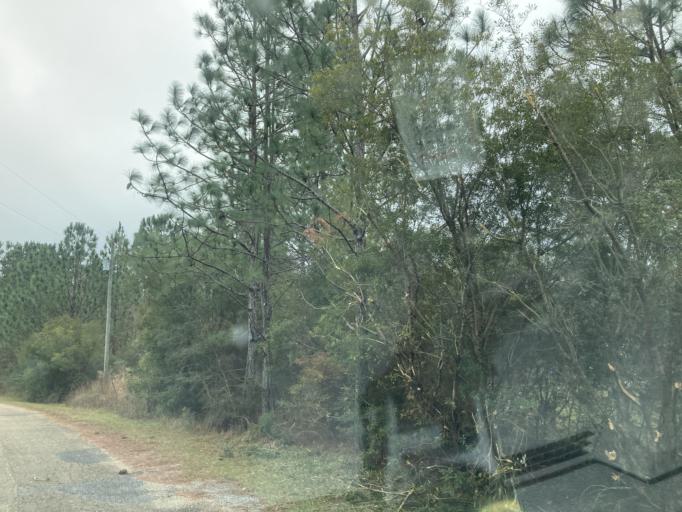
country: US
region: Mississippi
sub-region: Lamar County
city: Lumberton
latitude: 31.0178
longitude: -89.4965
